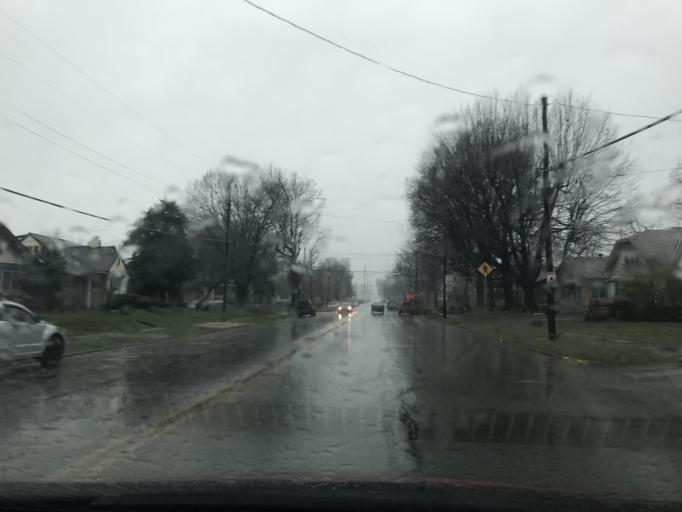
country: US
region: Indiana
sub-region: Clark County
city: Clarksville
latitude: 38.2871
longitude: -85.7643
